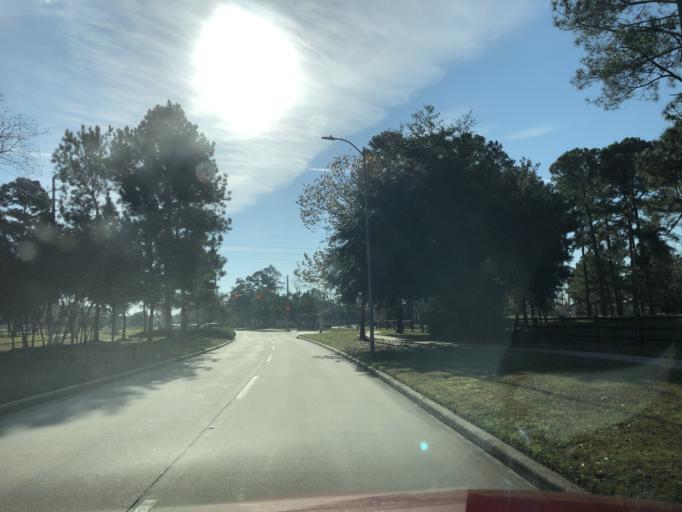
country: US
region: Texas
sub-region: Harris County
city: Tomball
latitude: 30.0378
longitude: -95.5621
